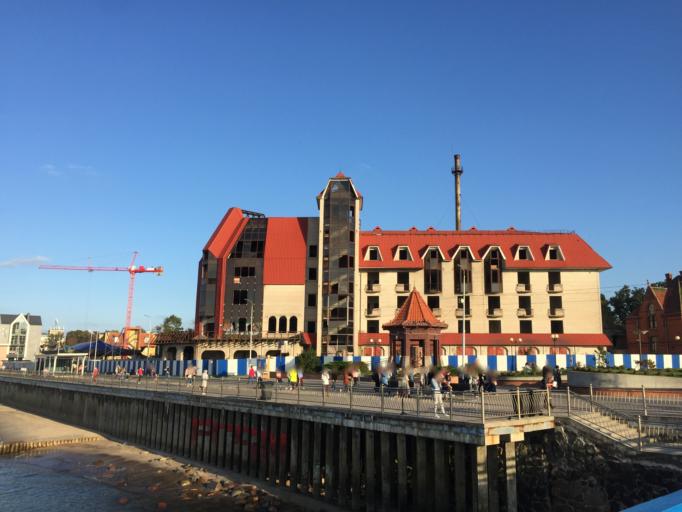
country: RU
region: Kaliningrad
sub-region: Zelenogradskiy Rayon
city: Zelenogradsk
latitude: 54.9623
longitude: 20.4747
